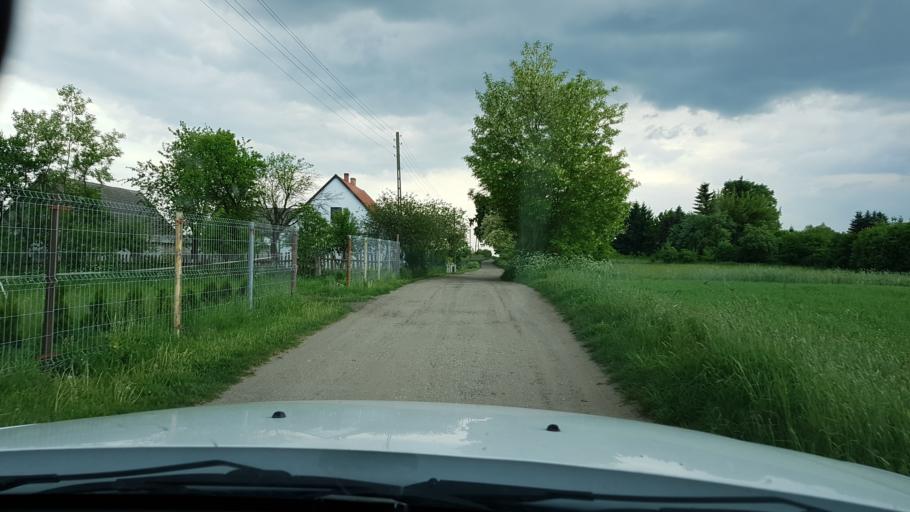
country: PL
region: West Pomeranian Voivodeship
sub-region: Powiat stargardzki
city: Stara Dabrowa
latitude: 53.3689
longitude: 15.1806
